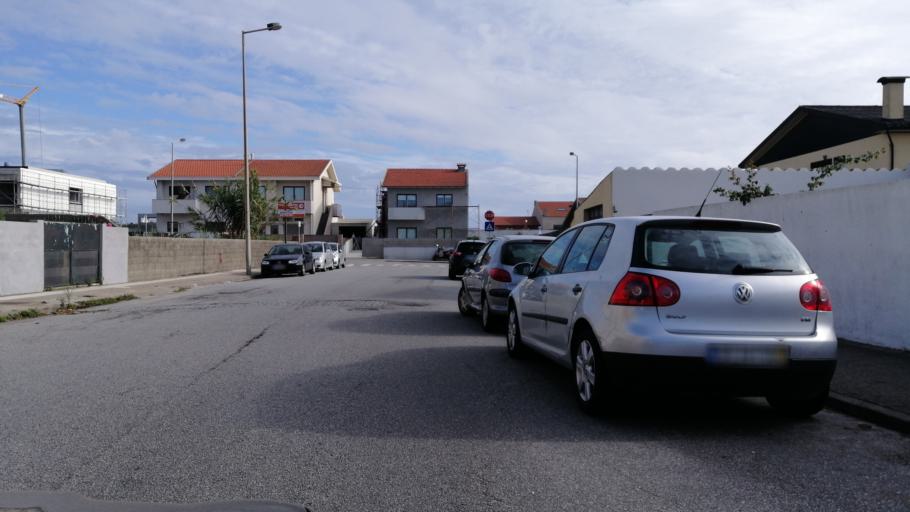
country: PT
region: Porto
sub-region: Matosinhos
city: Lavra
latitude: 41.2607
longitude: -8.7223
